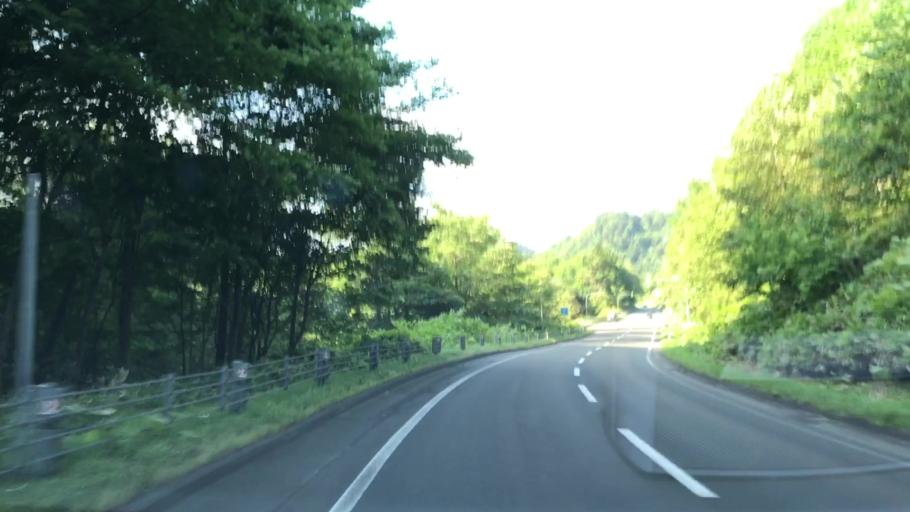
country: JP
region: Hokkaido
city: Iwamizawa
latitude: 42.8986
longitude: 142.1259
